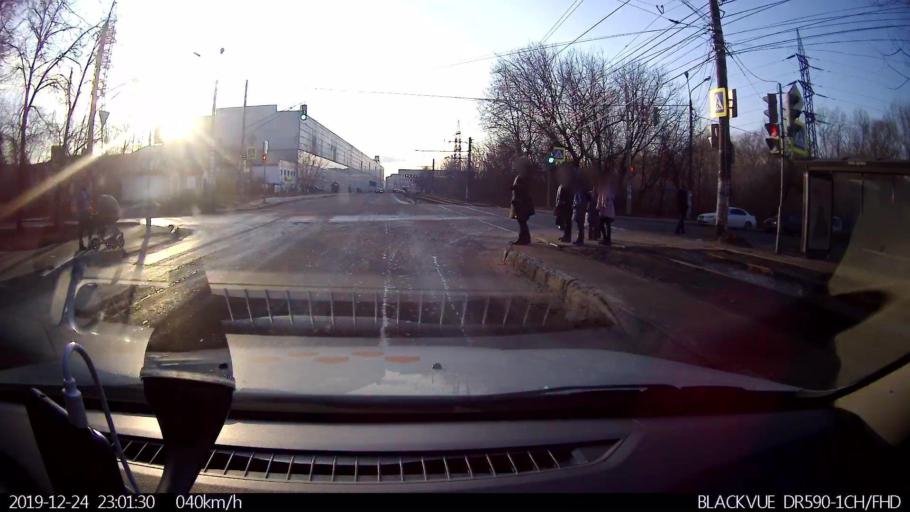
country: RU
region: Nizjnij Novgorod
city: Nizhniy Novgorod
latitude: 56.2678
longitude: 43.9262
